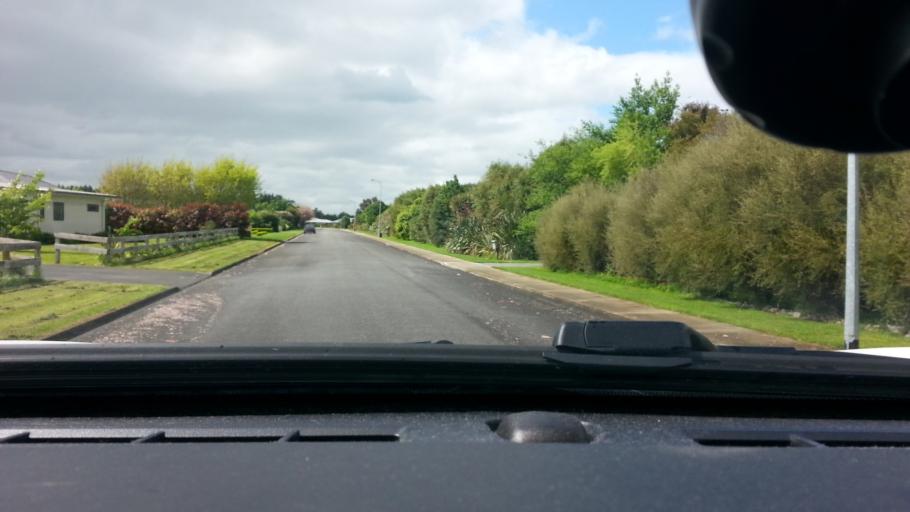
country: NZ
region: Wellington
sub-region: Masterton District
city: Masterton
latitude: -41.0174
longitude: 175.5192
